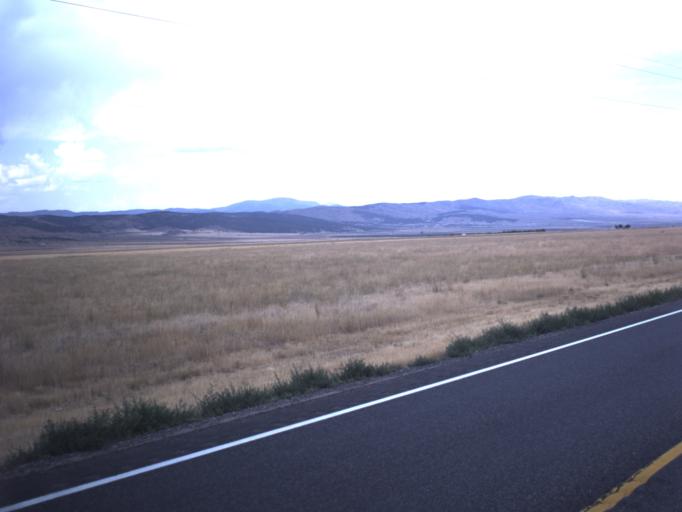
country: US
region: Utah
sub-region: Juab County
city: Nephi
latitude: 39.6275
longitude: -111.8617
